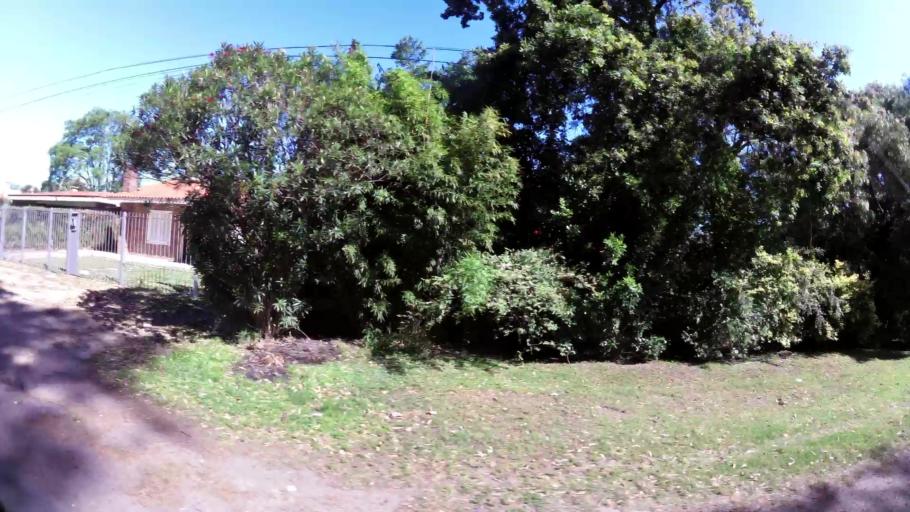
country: UY
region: Canelones
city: Barra de Carrasco
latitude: -34.8823
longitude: -56.0470
